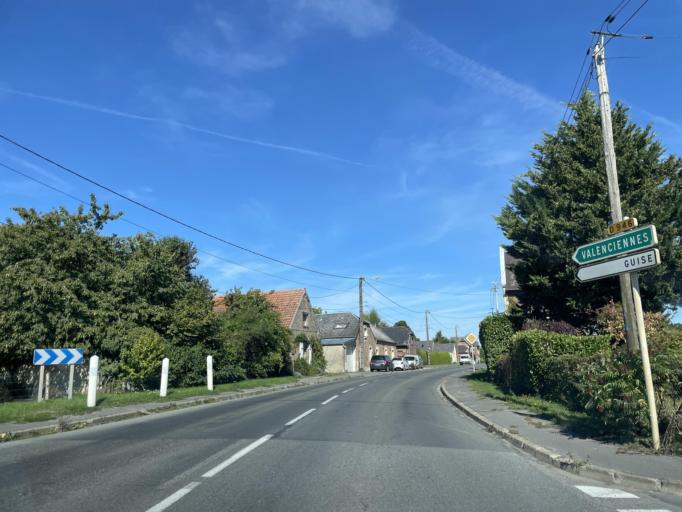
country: FR
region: Picardie
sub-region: Departement de l'Aisne
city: Guise
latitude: 49.8199
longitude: 3.6441
